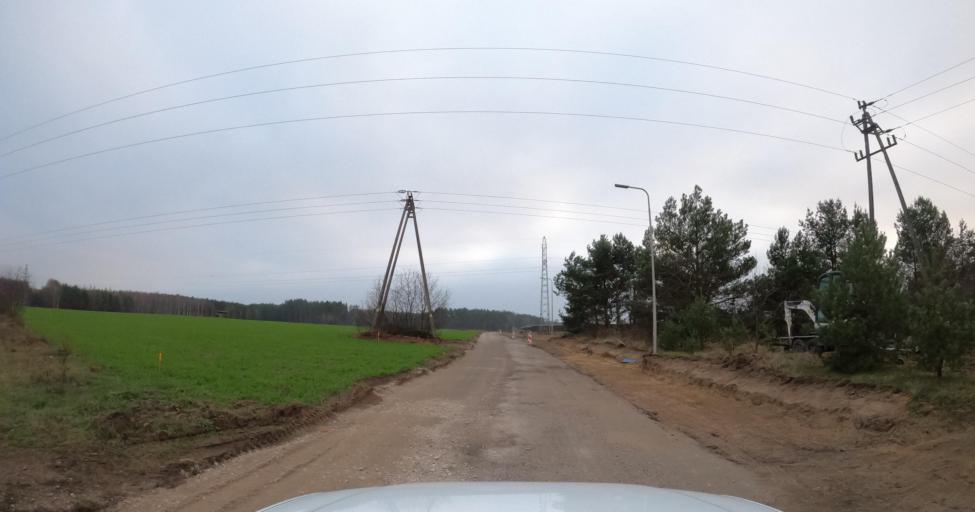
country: PL
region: West Pomeranian Voivodeship
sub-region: Powiat walecki
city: Miroslawiec
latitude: 53.3332
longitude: 16.0869
